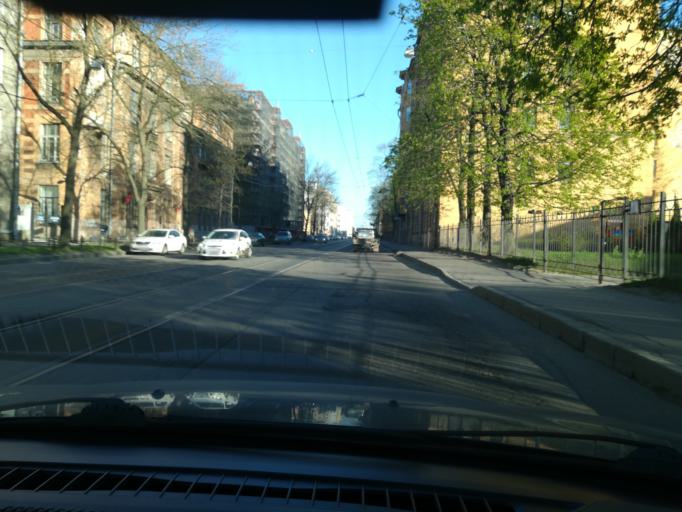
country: RU
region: St.-Petersburg
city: Vasyl'evsky Ostrov
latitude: 59.9349
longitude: 30.2605
